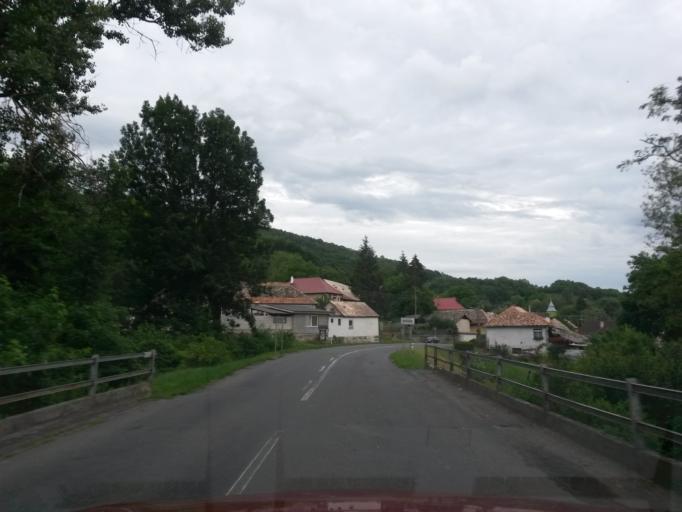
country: SK
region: Banskobystricky
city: Velky Krtis
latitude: 48.3013
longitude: 19.3993
